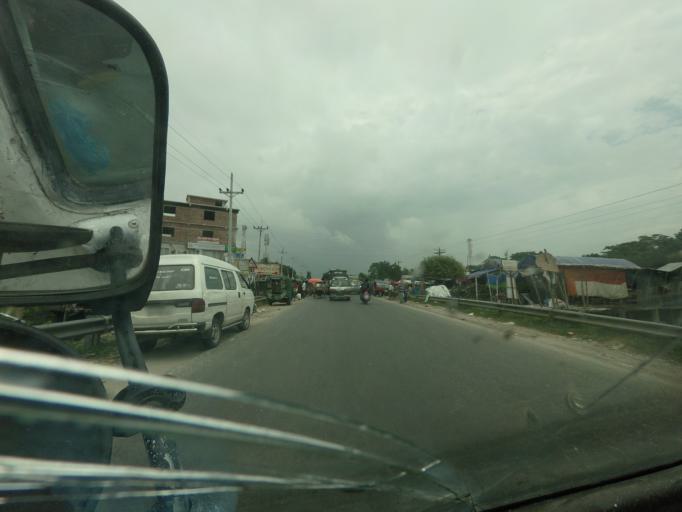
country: BD
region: Dhaka
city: Char Bhadrasan
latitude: 23.3718
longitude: 90.0325
